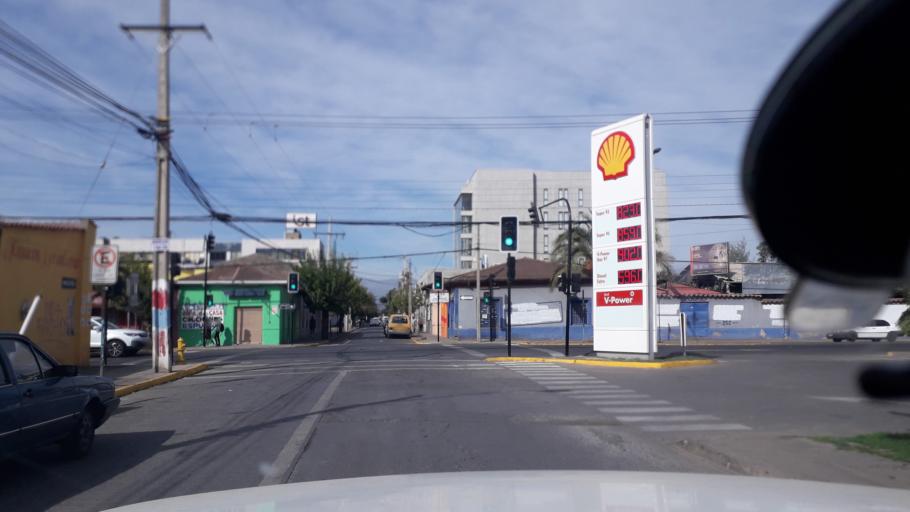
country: CL
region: Valparaiso
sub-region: Provincia de San Felipe
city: San Felipe
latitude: -32.7500
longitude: -70.7305
